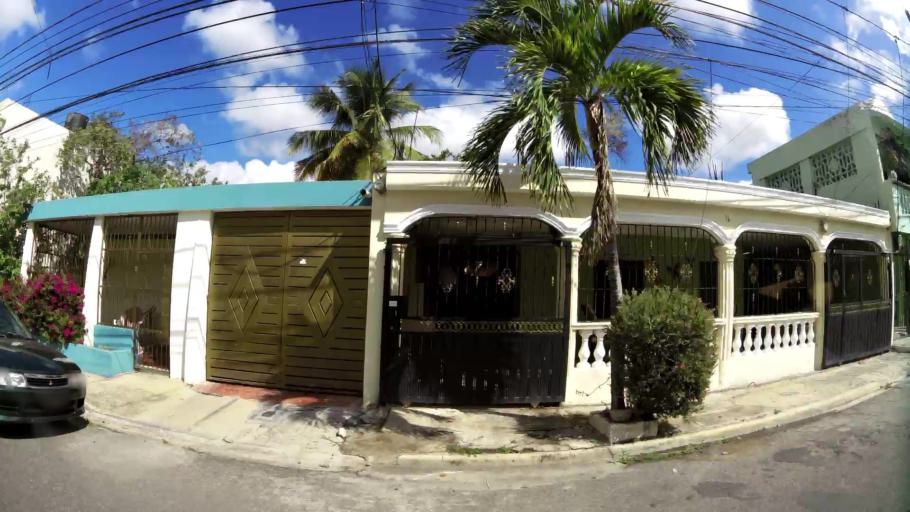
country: DO
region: Santo Domingo
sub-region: Santo Domingo
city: Santo Domingo Este
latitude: 18.5085
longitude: -69.8455
